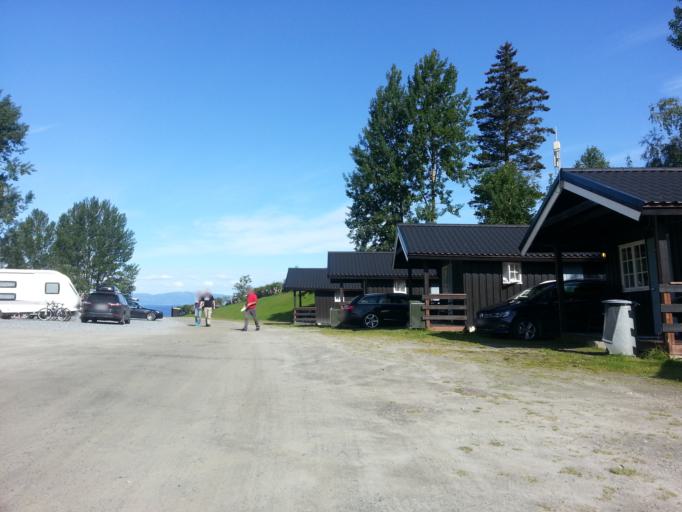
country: NO
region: Sor-Trondelag
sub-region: Malvik
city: Malvik
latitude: 63.4338
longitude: 10.7117
